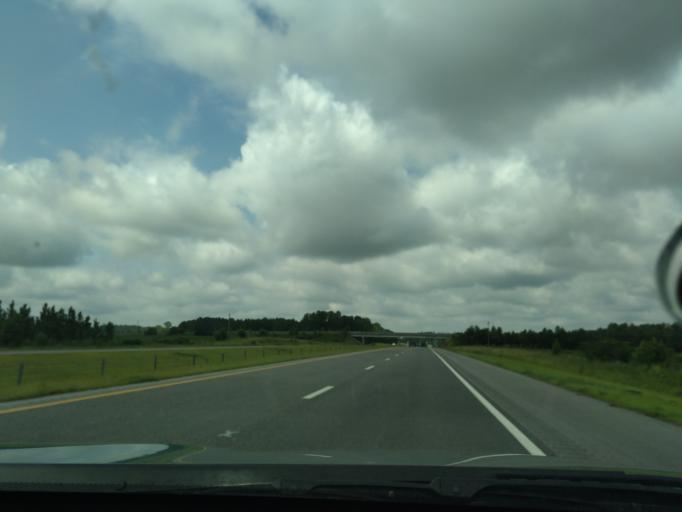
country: US
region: North Carolina
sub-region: Martin County
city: Robersonville
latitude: 35.8420
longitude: -77.2287
